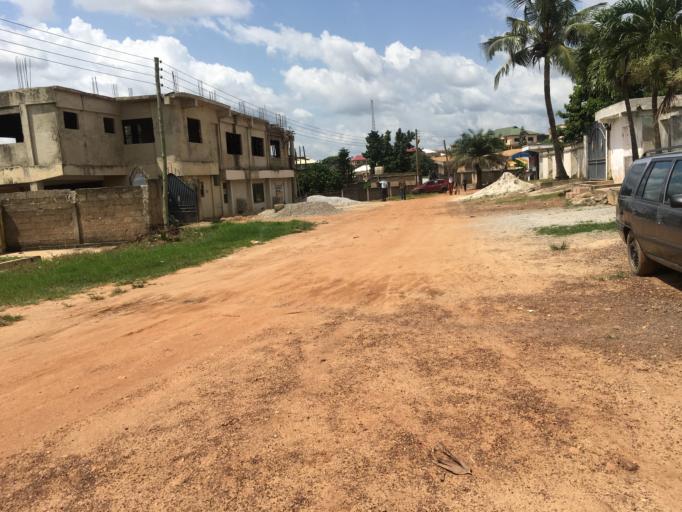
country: GH
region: Ashanti
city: Tafo
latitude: 6.7502
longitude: -1.5987
